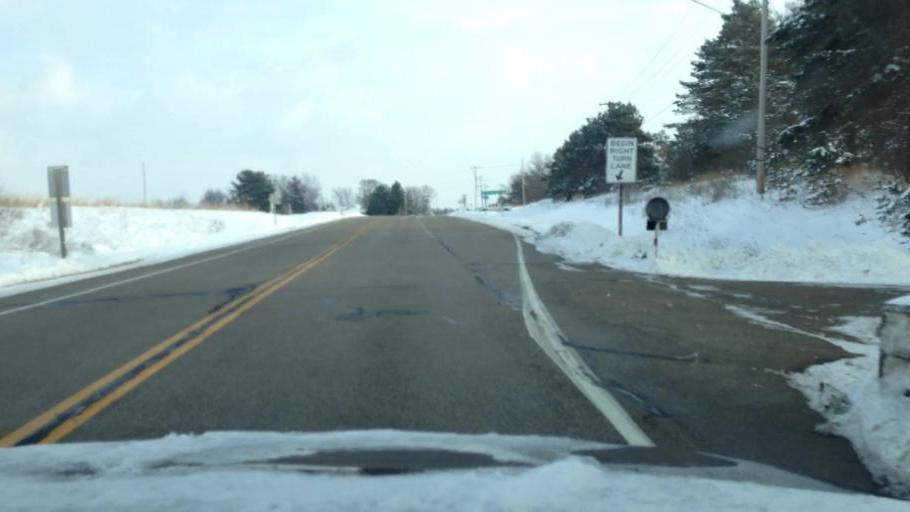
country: US
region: Wisconsin
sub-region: Walworth County
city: East Troy
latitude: 42.7924
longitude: -88.4272
